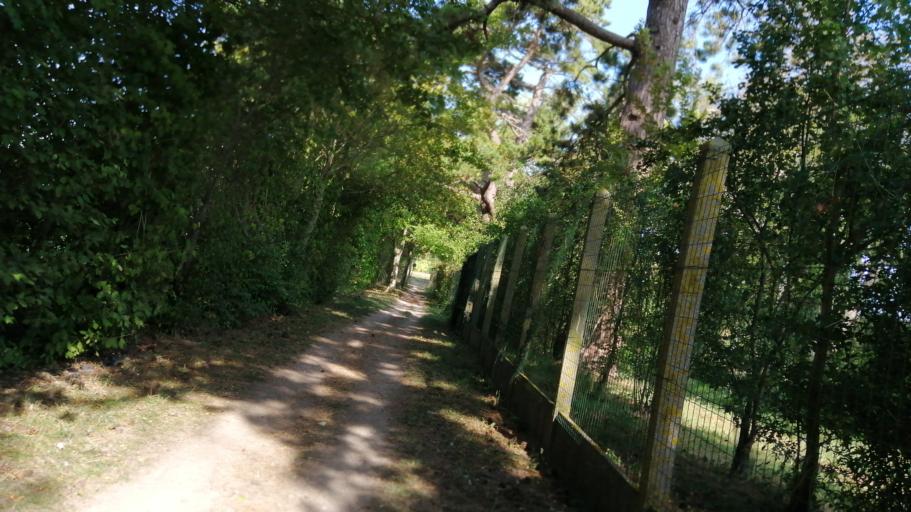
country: FR
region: Nord-Pas-de-Calais
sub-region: Departement du Pas-de-Calais
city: Dainville
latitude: 50.2853
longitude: 2.7122
